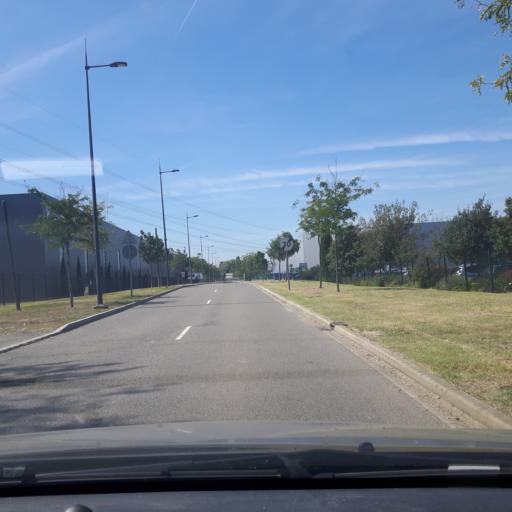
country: FR
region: Midi-Pyrenees
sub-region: Departement de la Haute-Garonne
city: Saint-Sauveur
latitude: 43.7639
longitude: 1.3843
